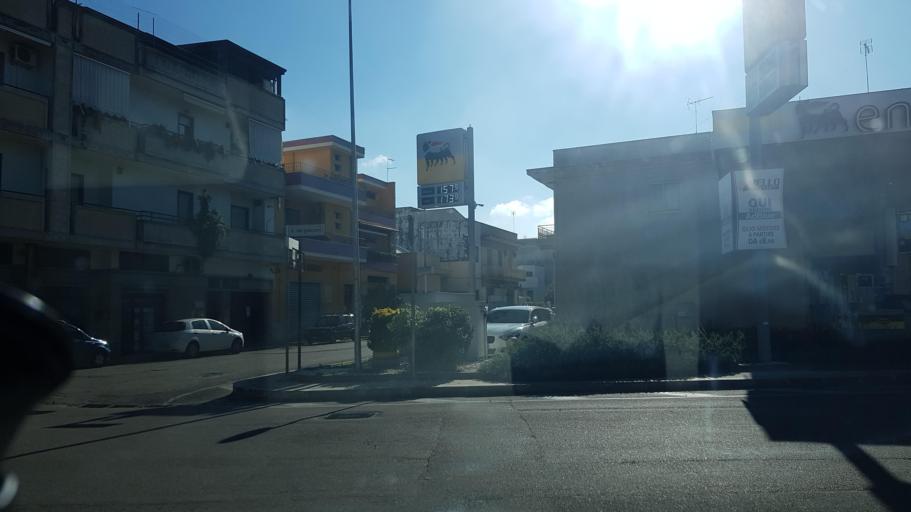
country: IT
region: Apulia
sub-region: Provincia di Lecce
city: Monteroni di Lecce
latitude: 40.3280
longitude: 18.1012
